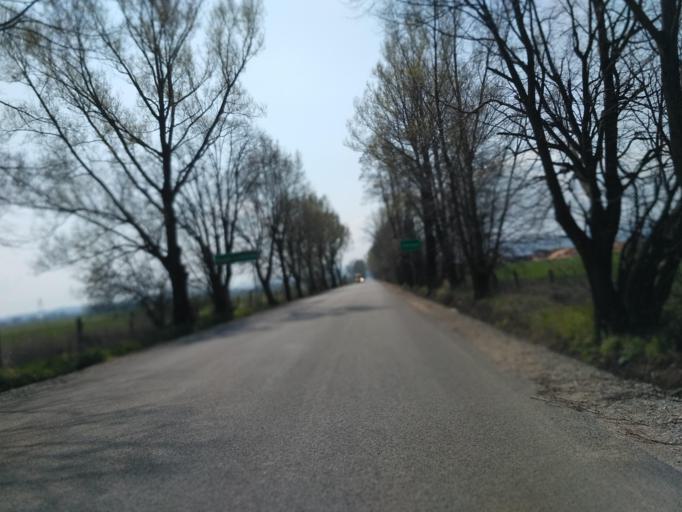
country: PL
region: Subcarpathian Voivodeship
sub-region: Powiat sanocki
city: Zarszyn
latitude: 49.5994
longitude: 22.0052
